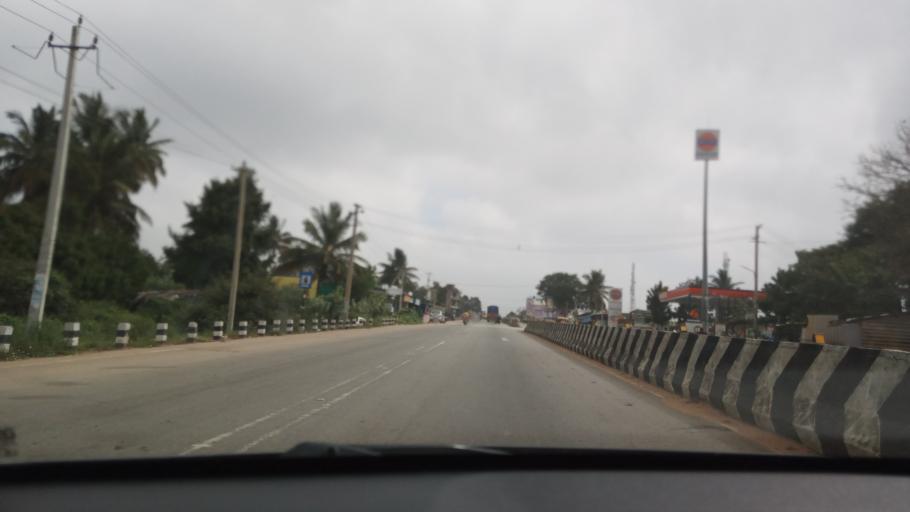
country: IN
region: Karnataka
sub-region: Chikkaballapur
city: Chintamani
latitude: 13.3567
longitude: 78.0347
